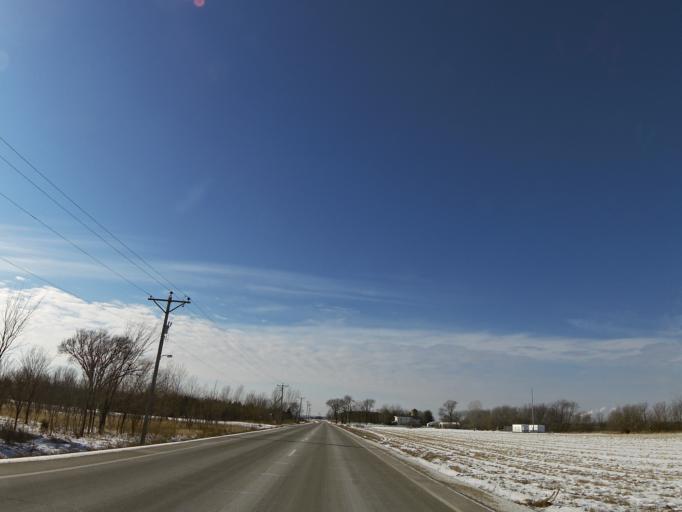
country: US
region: Wisconsin
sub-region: Saint Croix County
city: North Hudson
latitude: 44.9888
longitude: -92.6660
